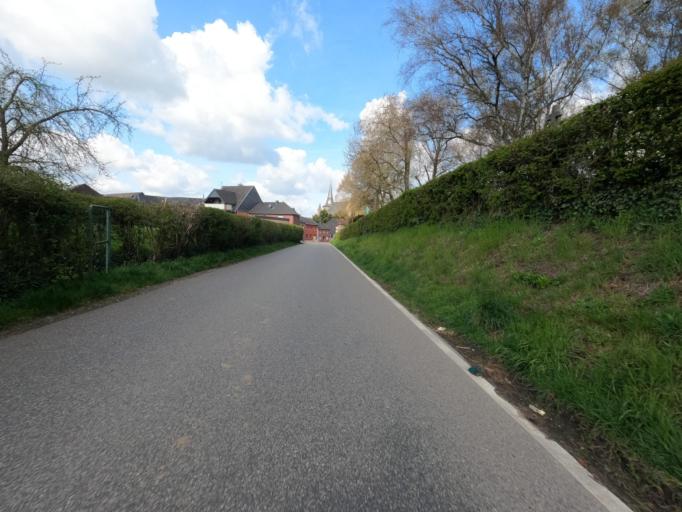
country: DE
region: North Rhine-Westphalia
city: Erkelenz
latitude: 51.0310
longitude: 6.3296
